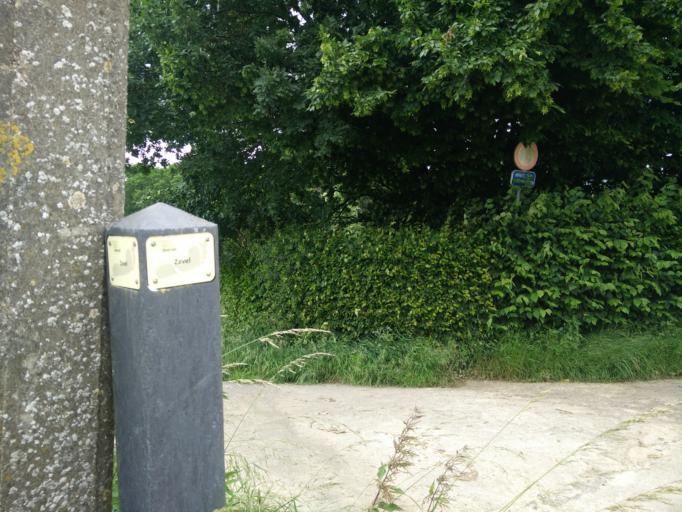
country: BE
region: Flanders
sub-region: Provincie Vlaams-Brabant
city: Beersel
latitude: 50.7478
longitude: 4.3139
